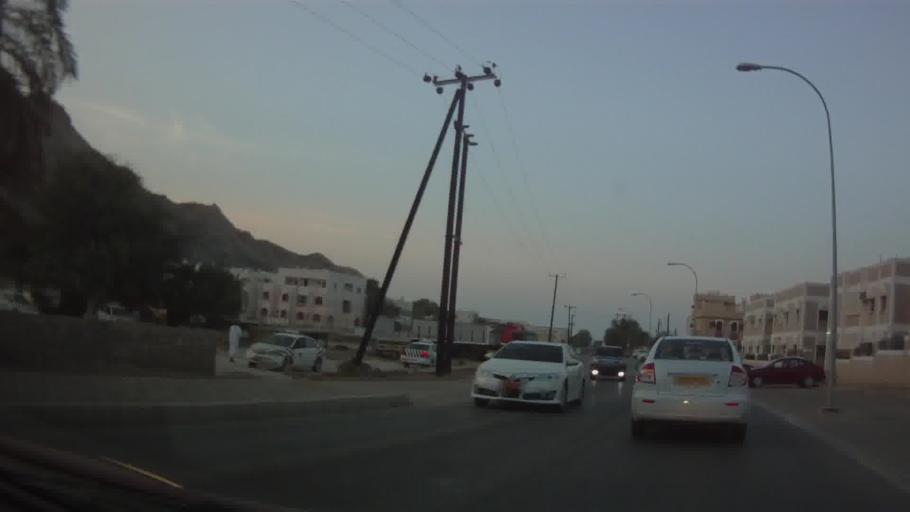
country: OM
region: Muhafazat Masqat
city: Muscat
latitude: 23.6238
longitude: 58.5411
